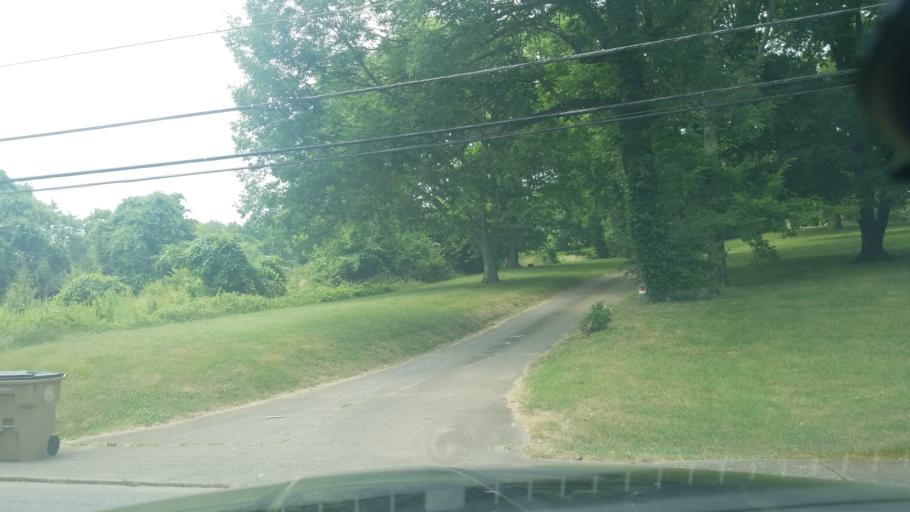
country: US
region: Tennessee
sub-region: Davidson County
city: Goodlettsville
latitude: 36.2526
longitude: -86.7434
